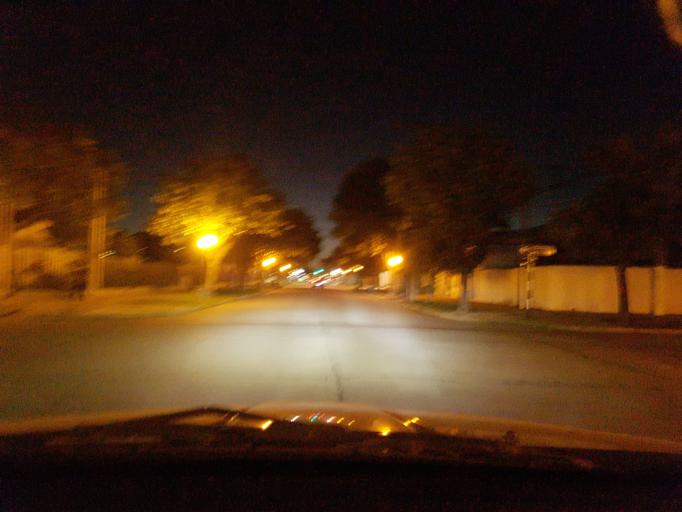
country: AR
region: Cordoba
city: Las Perdices
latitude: -32.7549
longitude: -63.7878
